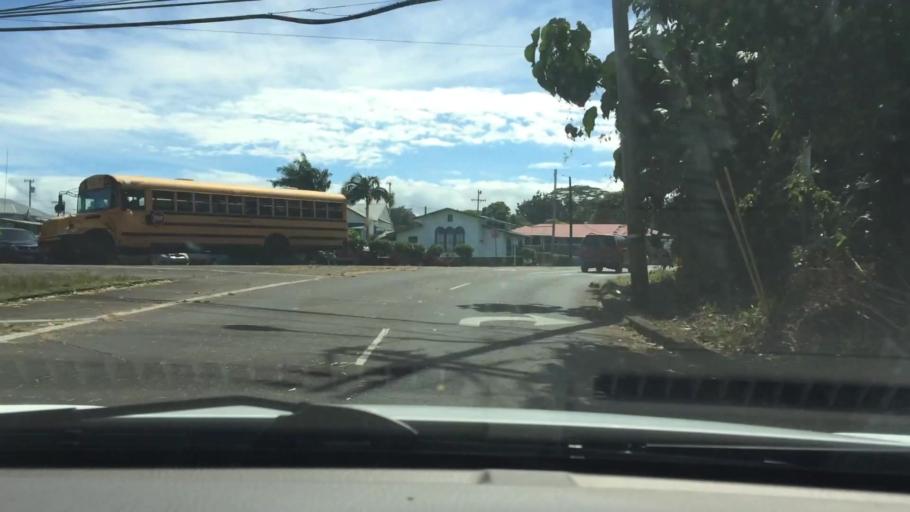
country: US
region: Hawaii
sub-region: Hawaii County
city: Hilo
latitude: 19.7262
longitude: -155.0896
